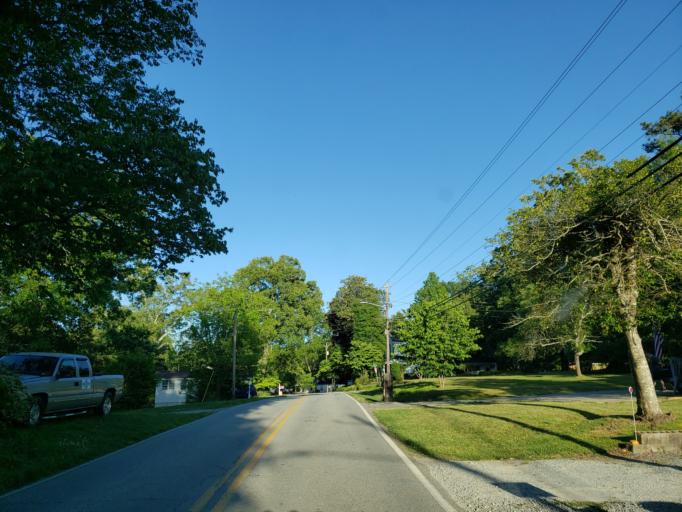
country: US
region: Georgia
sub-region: Haralson County
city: Tallapoosa
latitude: 33.7545
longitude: -85.3020
